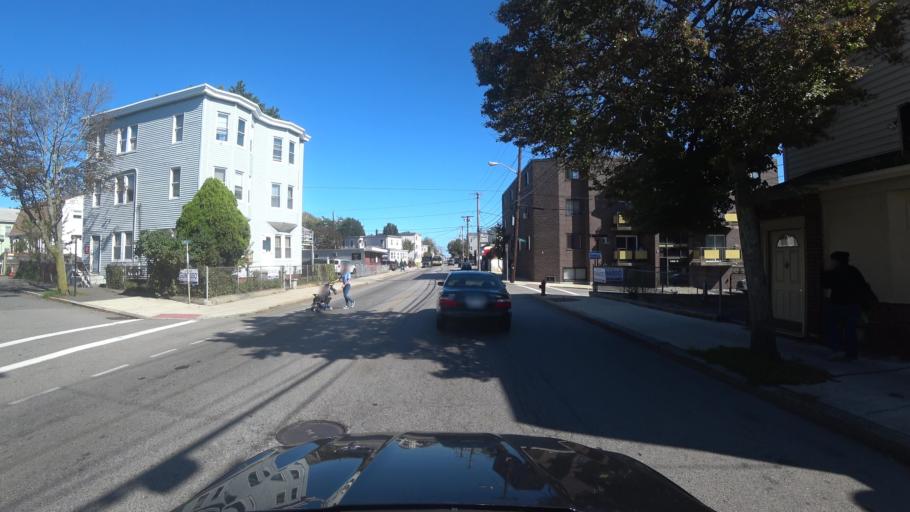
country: US
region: Massachusetts
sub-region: Suffolk County
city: Revere
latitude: 42.4185
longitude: -70.9982
